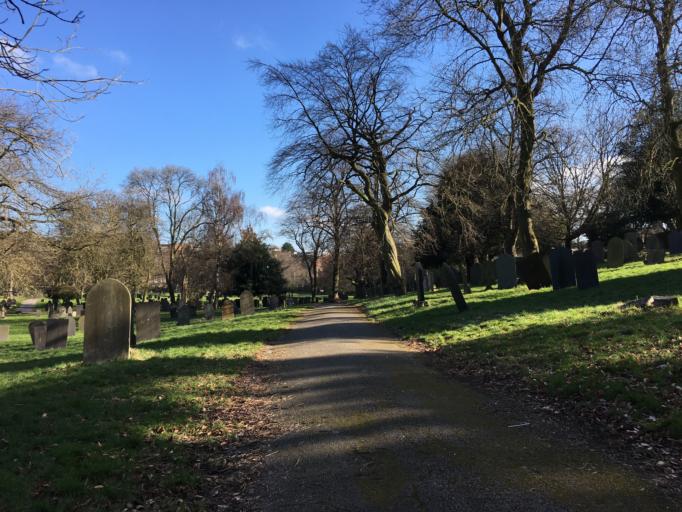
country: GB
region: England
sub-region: Nottingham
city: Nottingham
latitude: 52.9577
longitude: -1.1595
